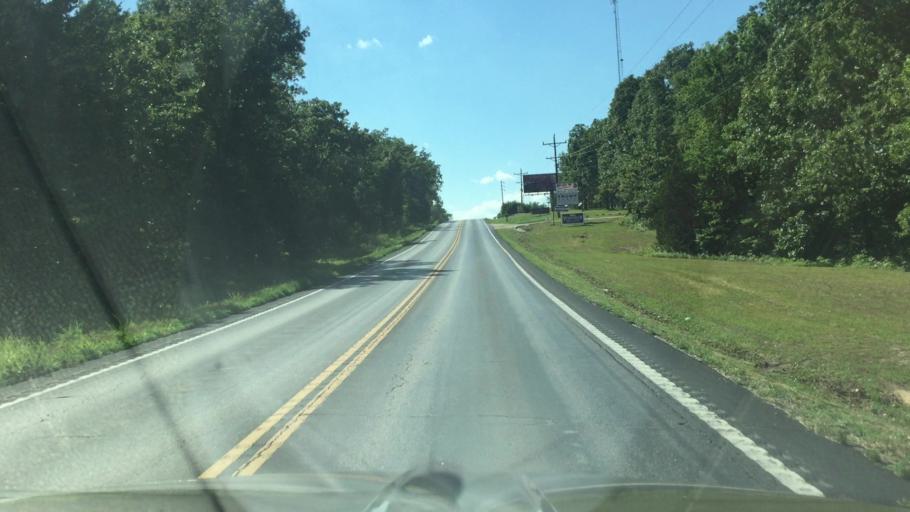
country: US
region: Missouri
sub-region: Camden County
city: Osage Beach
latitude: 38.1364
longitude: -92.5737
